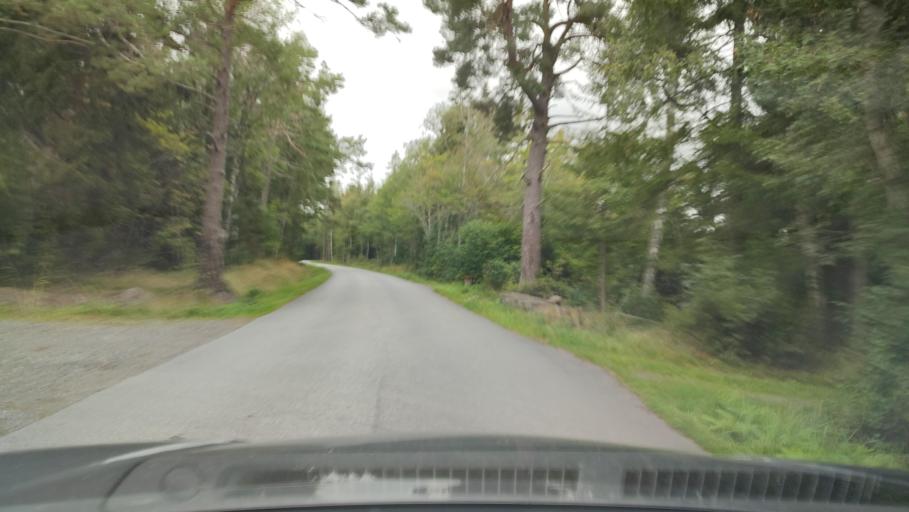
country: FI
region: Ostrobothnia
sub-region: Sydosterbotten
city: Kristinestad
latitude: 62.2551
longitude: 21.3557
